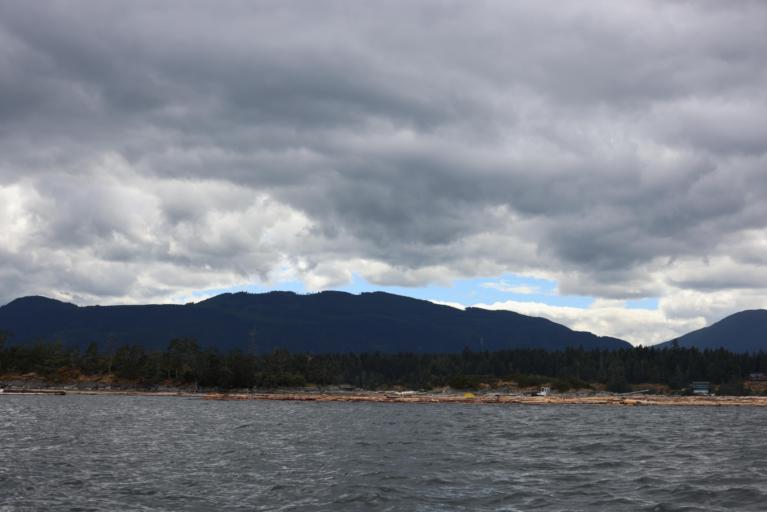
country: CA
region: British Columbia
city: North Cowichan
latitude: 48.9159
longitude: -123.6819
